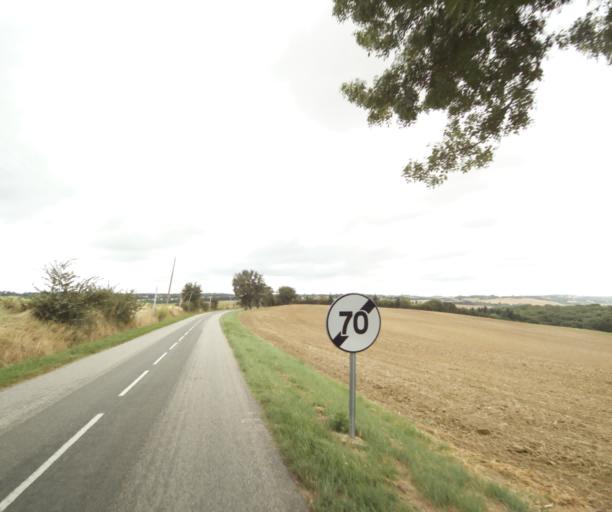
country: FR
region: Midi-Pyrenees
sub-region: Departement de la Haute-Garonne
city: Flourens
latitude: 43.6012
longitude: 1.5508
